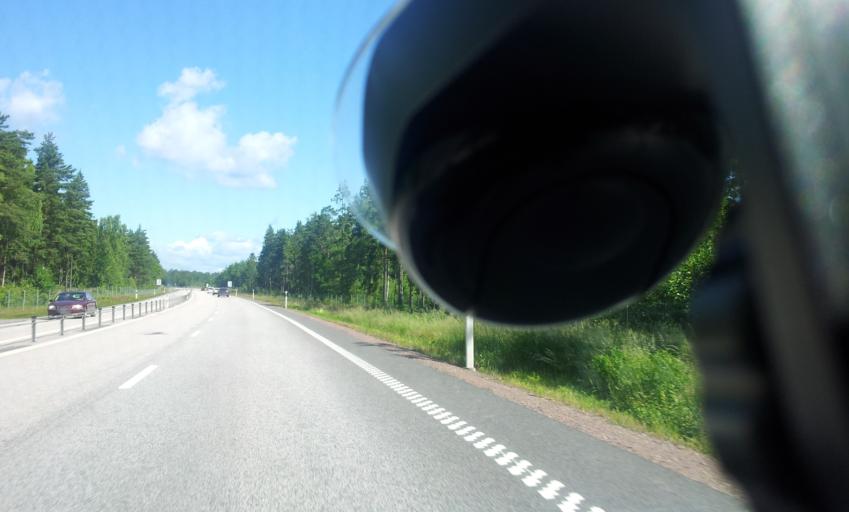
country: SE
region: Kalmar
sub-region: Oskarshamns Kommun
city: Paskallavik
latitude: 57.1061
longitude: 16.4989
